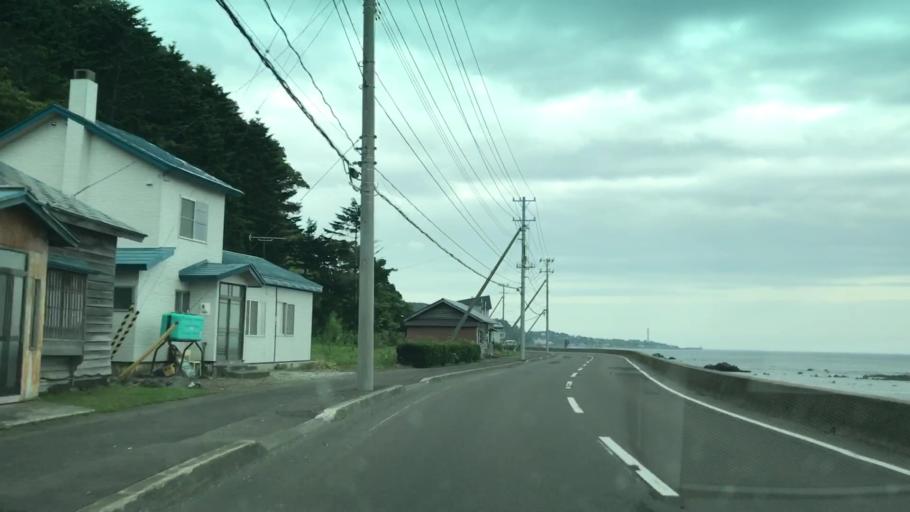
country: JP
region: Hokkaido
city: Iwanai
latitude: 42.7689
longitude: 140.2451
